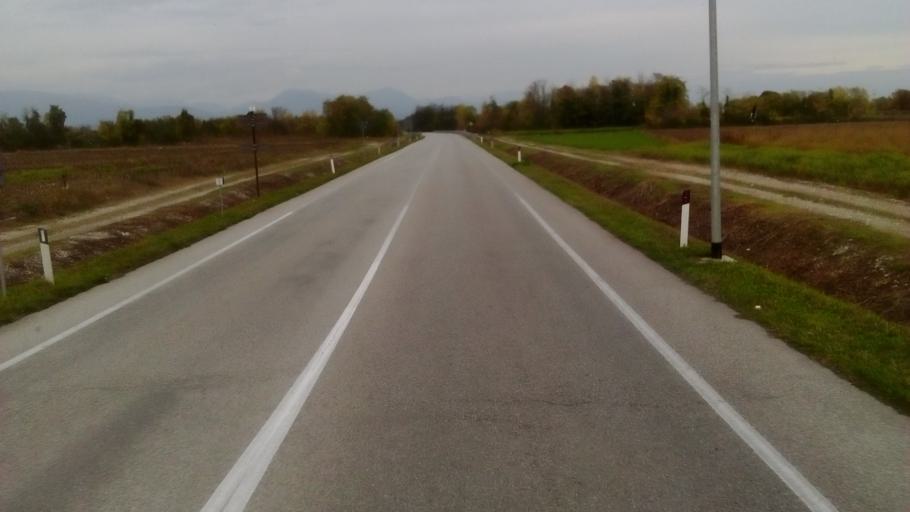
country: IT
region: Friuli Venezia Giulia
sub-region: Provincia di Pordenone
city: Vivaro
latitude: 46.0834
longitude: 12.7729
